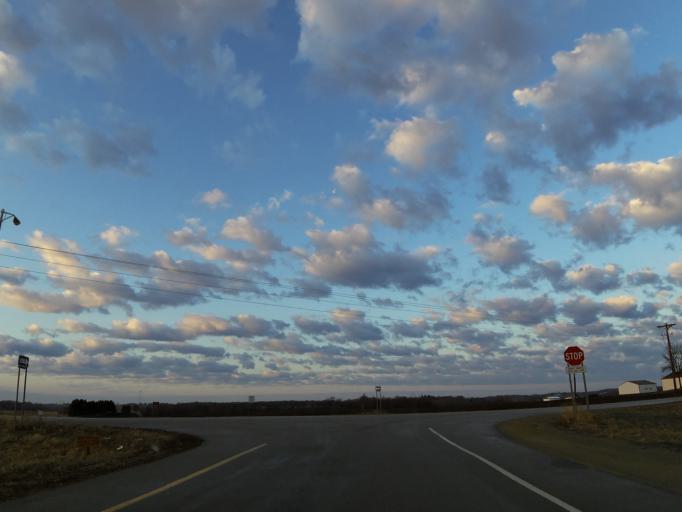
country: US
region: Minnesota
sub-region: Rice County
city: Dundas
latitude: 44.4289
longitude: -93.2943
